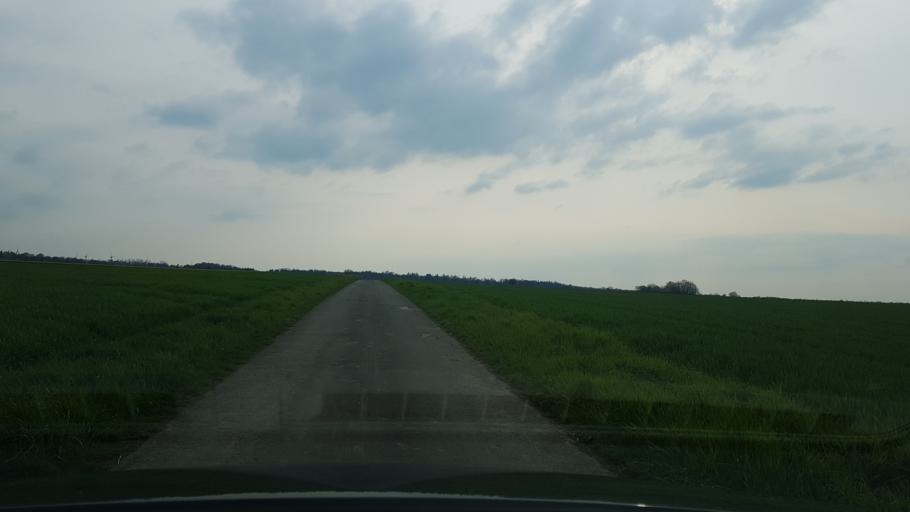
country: DE
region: North Rhine-Westphalia
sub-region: Regierungsbezirk Detmold
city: Paderborn
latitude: 51.6235
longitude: 8.7449
